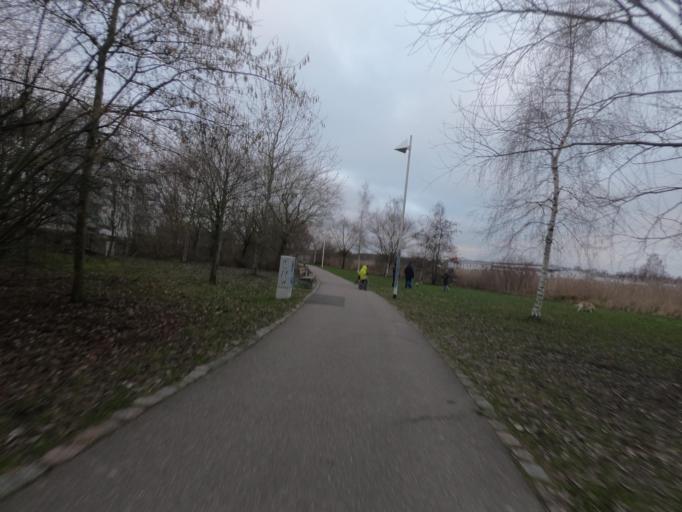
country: DE
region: Mecklenburg-Vorpommern
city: Rostock
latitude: 54.0930
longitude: 12.1522
